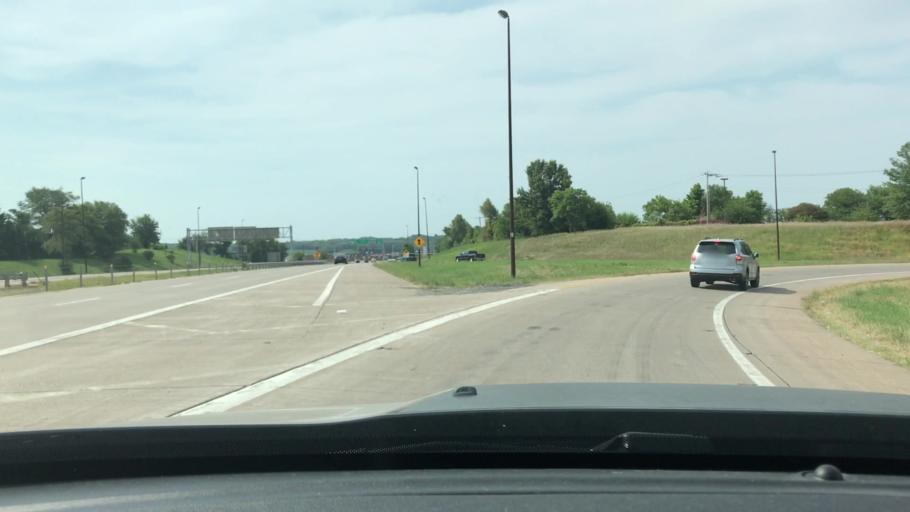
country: US
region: Illinois
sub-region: Rock Island County
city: Coal Valley
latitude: 41.4570
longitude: -90.4954
